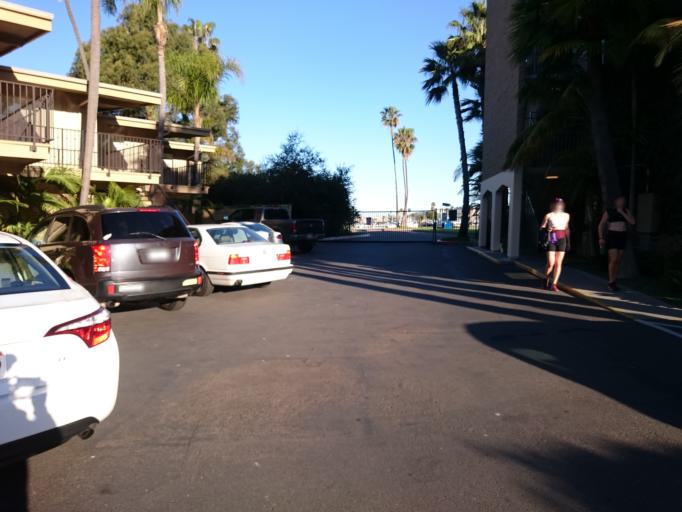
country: US
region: California
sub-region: San Diego County
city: La Jolla
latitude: 32.7747
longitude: -117.2467
